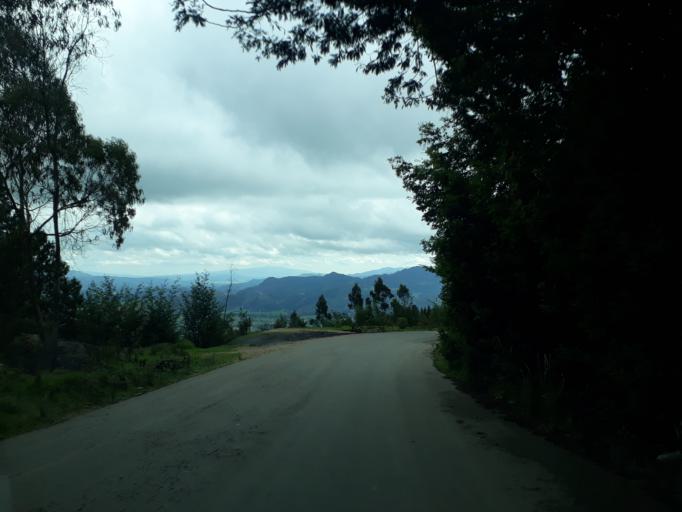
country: CO
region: Cundinamarca
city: Cucunuba
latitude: 5.2075
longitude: -73.7891
